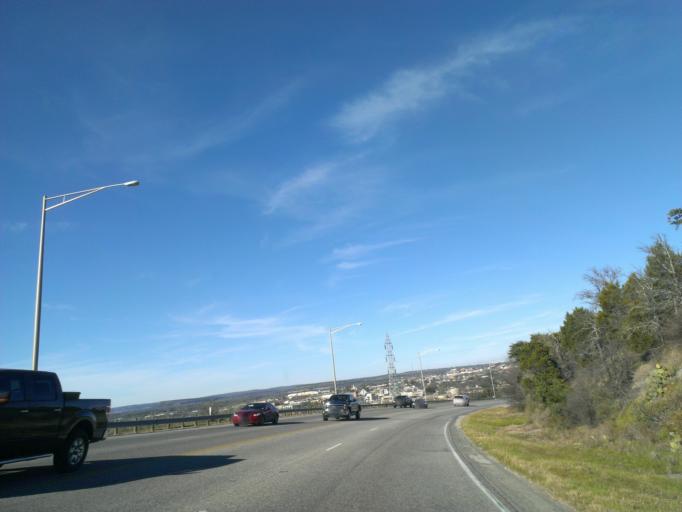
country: US
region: Texas
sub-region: Burnet County
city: Marble Falls
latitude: 30.5607
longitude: -98.2761
